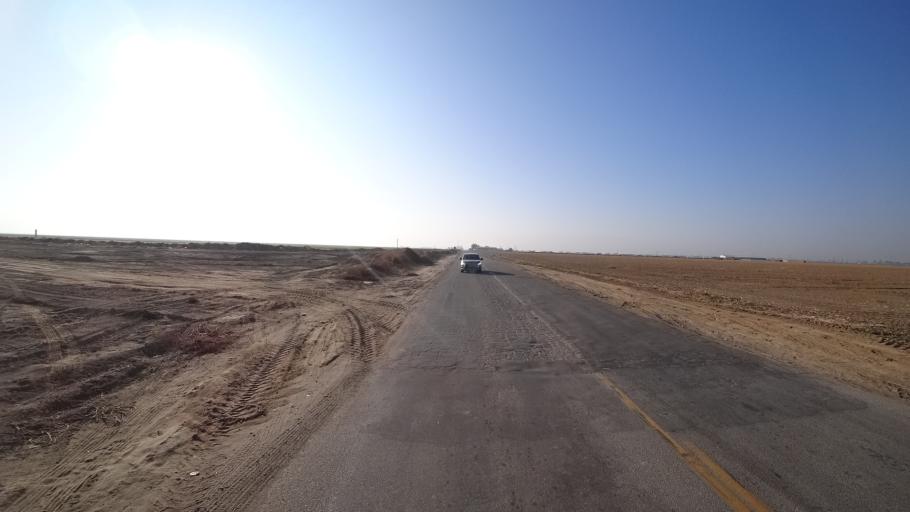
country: US
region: California
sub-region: Kern County
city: Greenfield
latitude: 35.2376
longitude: -118.9677
